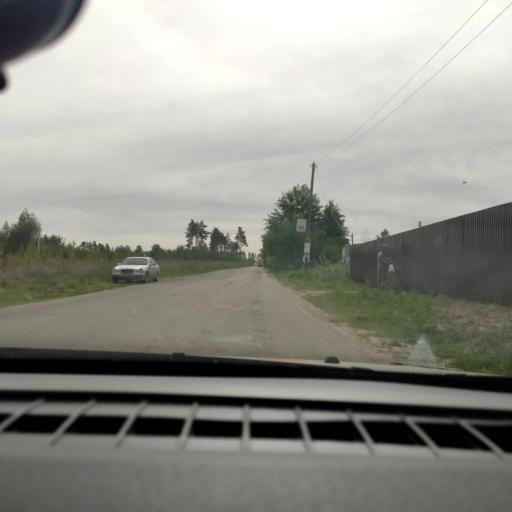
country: RU
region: Voronezj
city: Podgornoye
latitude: 51.8395
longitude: 39.1904
